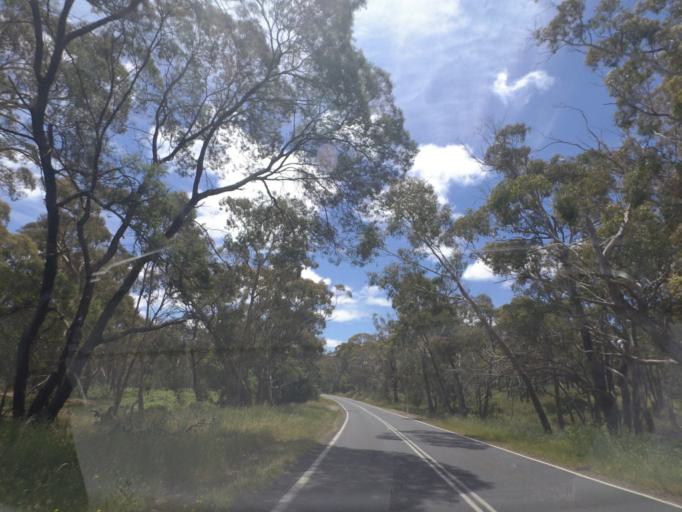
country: AU
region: Victoria
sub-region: Mount Alexander
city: Castlemaine
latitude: -37.3152
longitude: 144.1662
